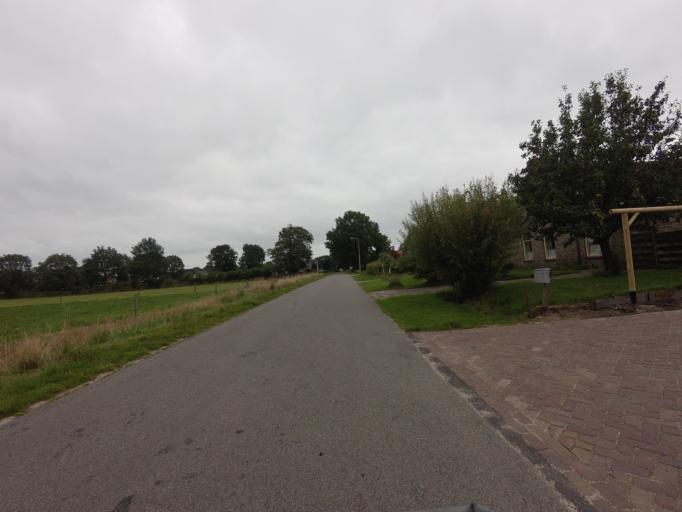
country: NL
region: Overijssel
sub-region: Gemeente Steenwijkerland
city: Steenwijkerwold
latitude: 52.7999
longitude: 6.0504
